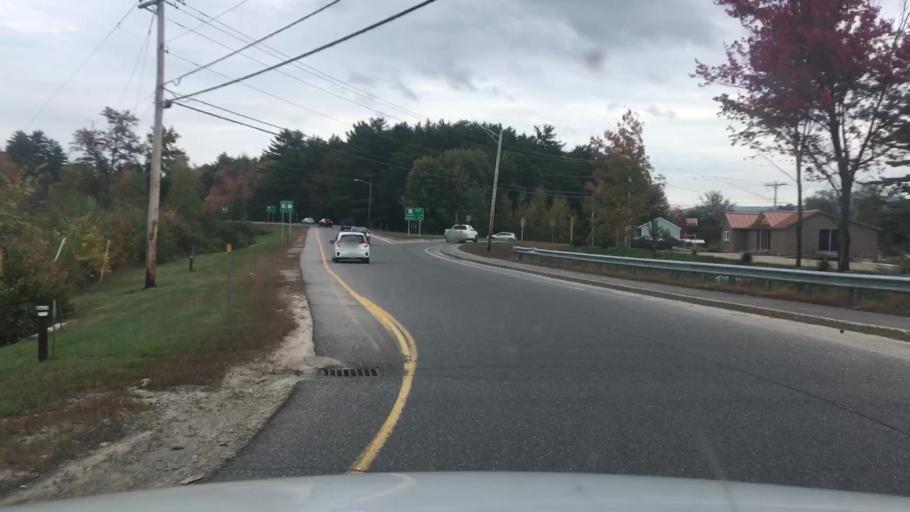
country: US
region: New Hampshire
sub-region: Strafford County
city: New Durham
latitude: 43.4515
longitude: -71.2121
